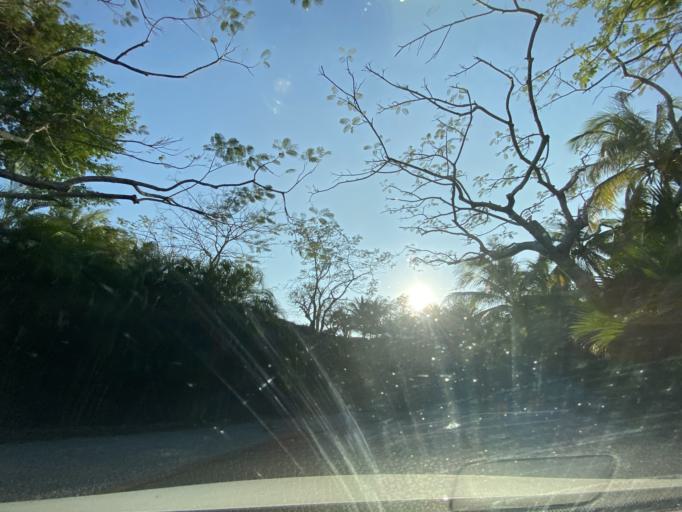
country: CN
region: Hainan
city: Xincun
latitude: 18.4182
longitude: 109.9515
